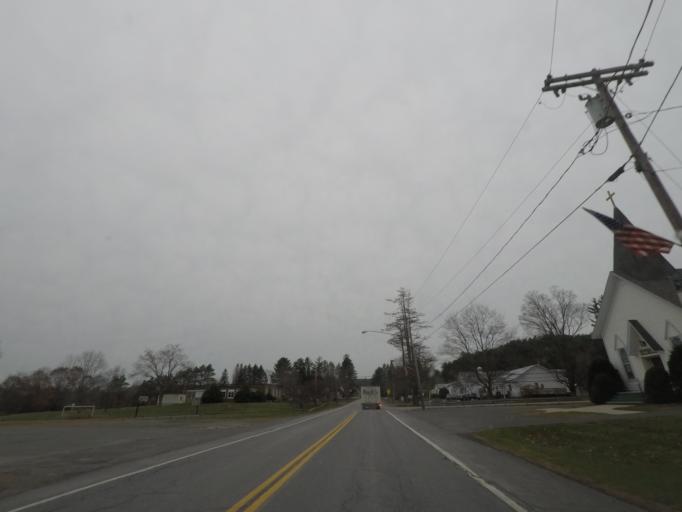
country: US
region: Massachusetts
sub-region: Berkshire County
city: Lanesborough
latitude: 42.5501
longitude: -73.3798
